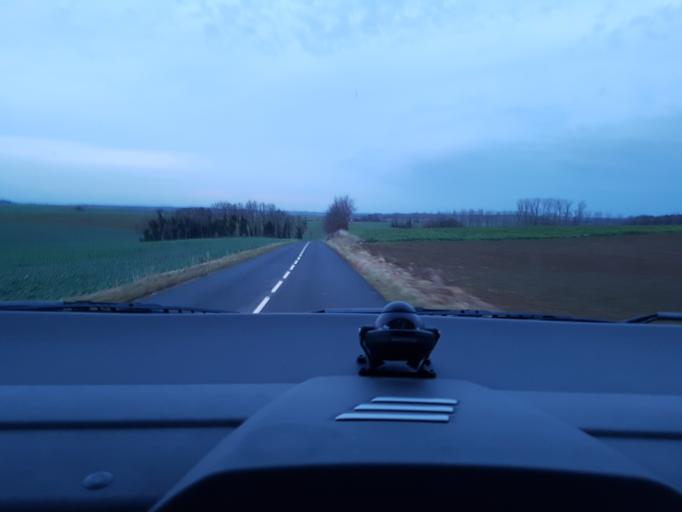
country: FR
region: Picardie
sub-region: Departement de la Somme
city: Beauquesne
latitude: 50.0751
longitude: 2.4223
